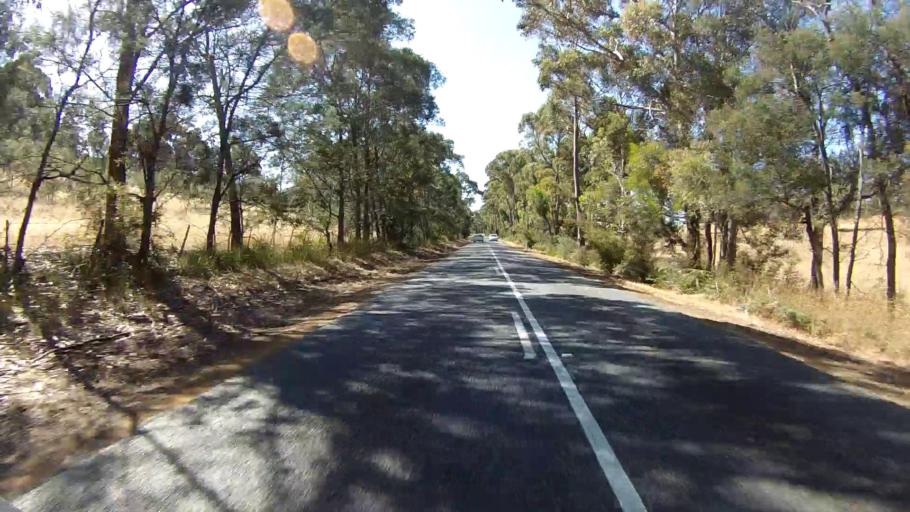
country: AU
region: Tasmania
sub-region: Sorell
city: Sorell
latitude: -42.3149
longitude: 147.9604
